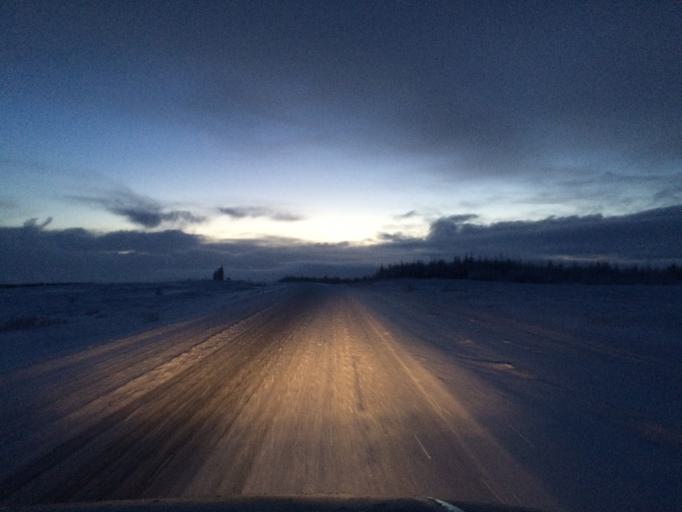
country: IS
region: South
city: Selfoss
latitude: 64.0843
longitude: -20.7465
